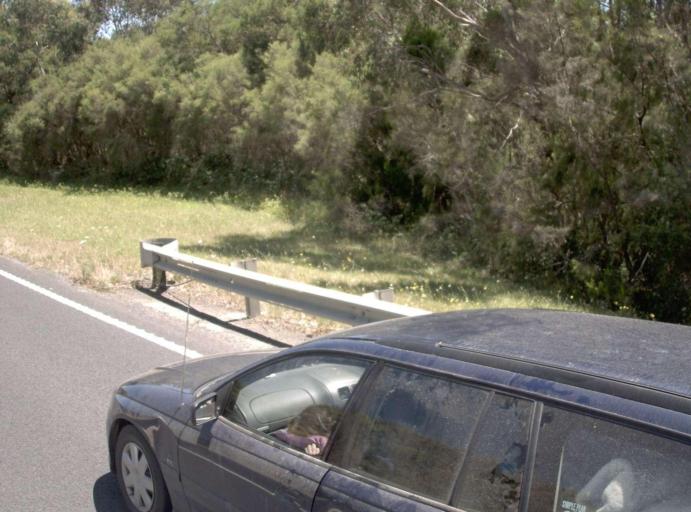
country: AU
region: Victoria
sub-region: Cardinia
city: Pakenham Upper
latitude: -38.0701
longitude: 145.5848
